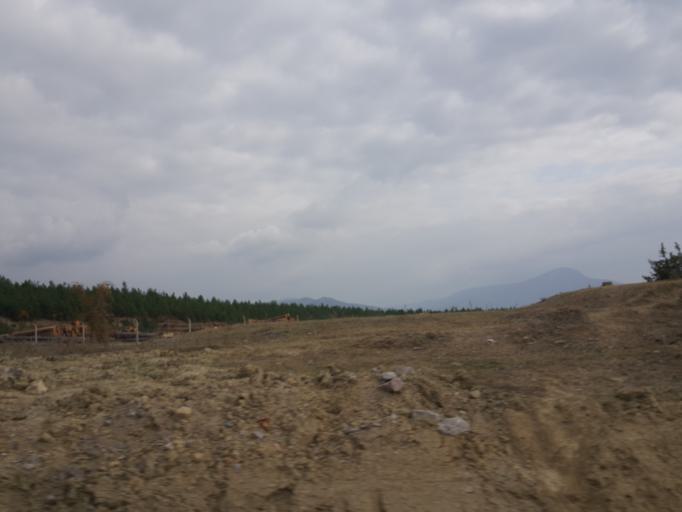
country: TR
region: Sinop
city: Duragan
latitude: 41.4322
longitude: 35.0540
